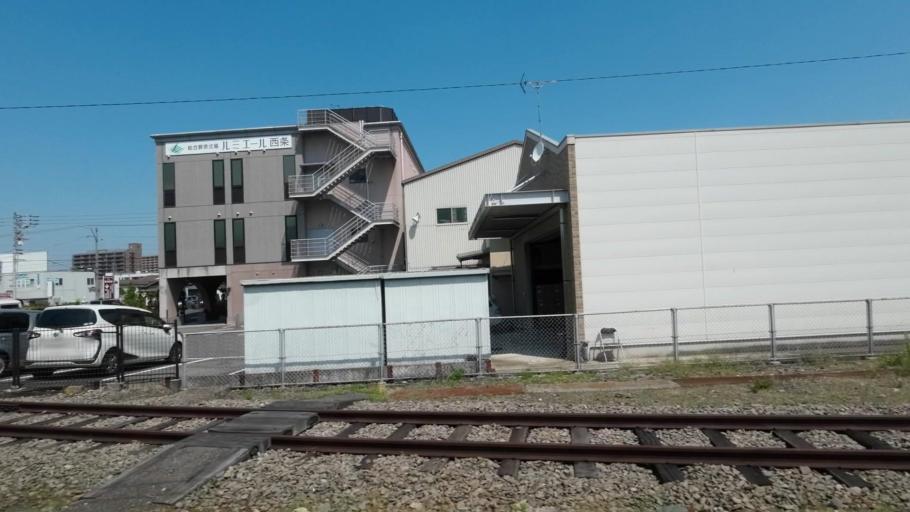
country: JP
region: Ehime
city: Saijo
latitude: 33.9130
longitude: 133.1891
